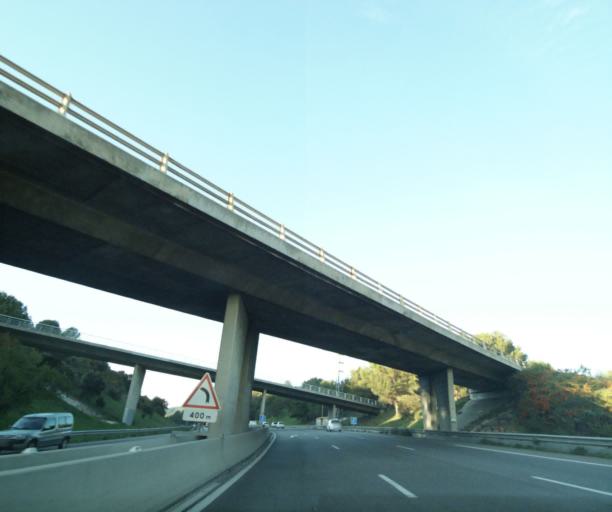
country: FR
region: Provence-Alpes-Cote d'Azur
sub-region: Departement des Bouches-du-Rhone
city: Roquevaire
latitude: 43.3527
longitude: 5.6209
